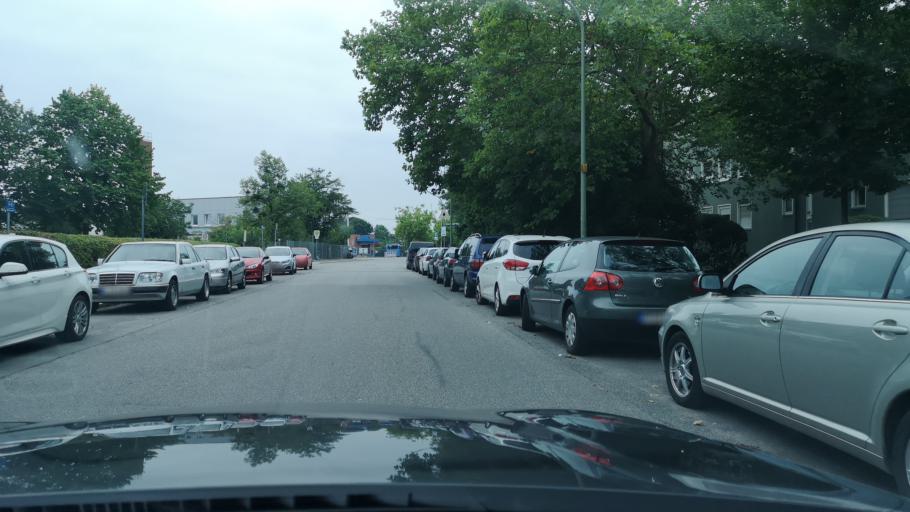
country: DE
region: Bavaria
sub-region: Upper Bavaria
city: Munich
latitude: 48.1346
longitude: 11.5173
